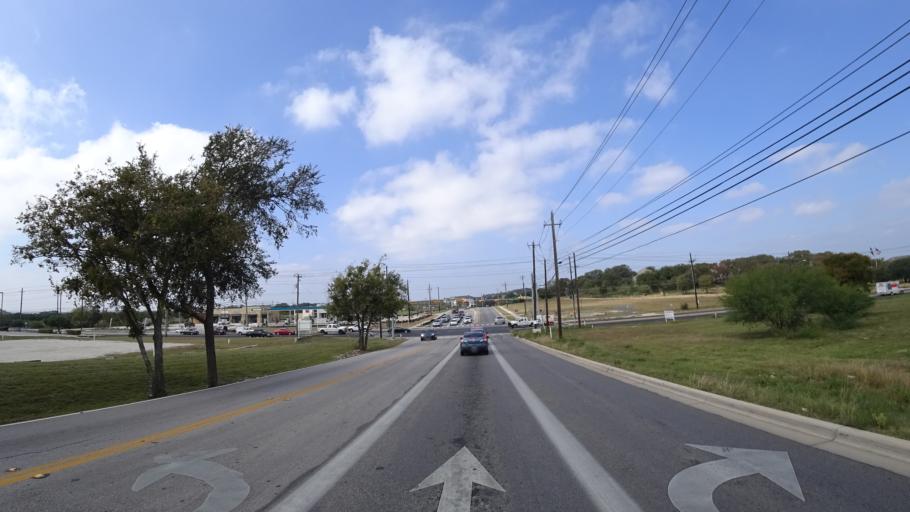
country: US
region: Texas
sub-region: Travis County
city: Shady Hollow
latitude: 30.1950
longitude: -97.8416
